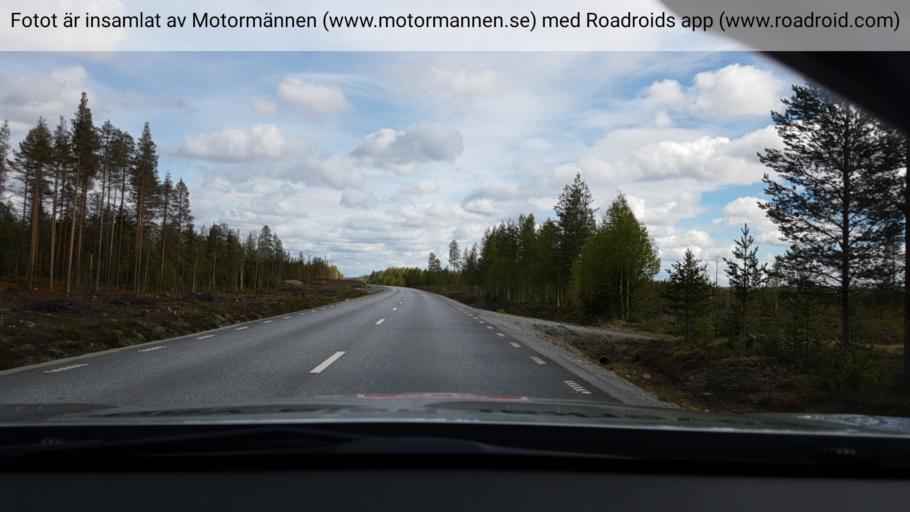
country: SE
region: Vaesternorrland
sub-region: OErnskoeldsviks Kommun
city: Bredbyn
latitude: 64.1198
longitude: 18.0963
